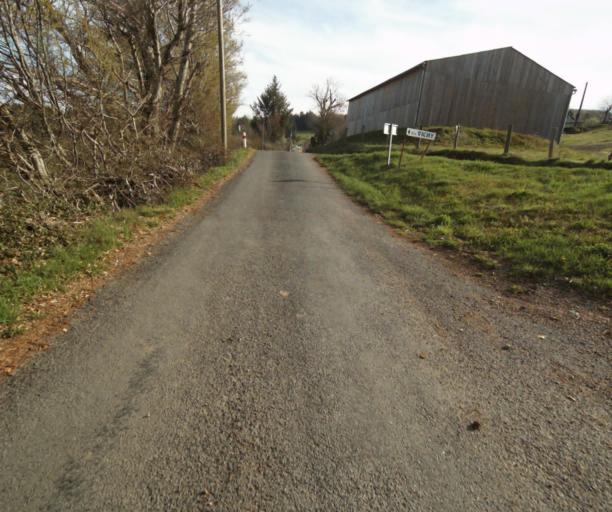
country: FR
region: Limousin
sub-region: Departement de la Correze
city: Naves
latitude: 45.3275
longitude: 1.8259
